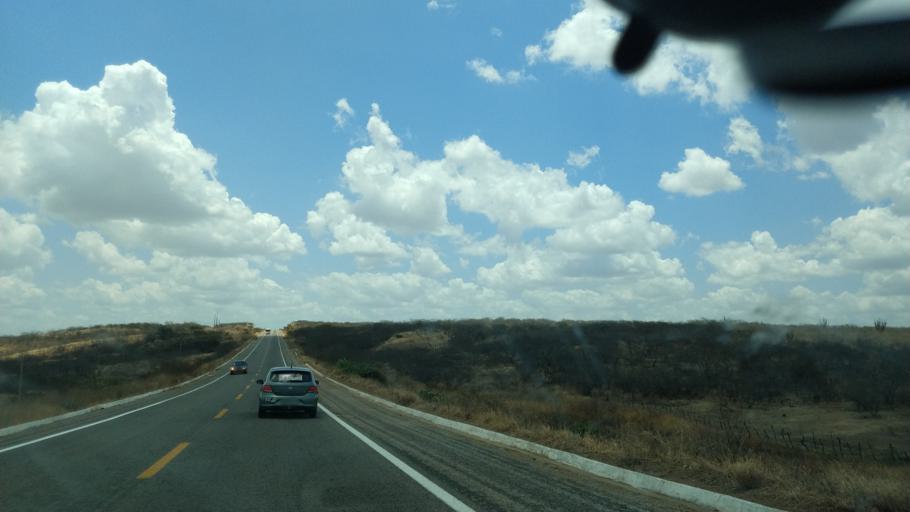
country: BR
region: Rio Grande do Norte
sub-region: Cerro Cora
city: Cerro Cora
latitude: -6.2017
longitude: -36.3341
